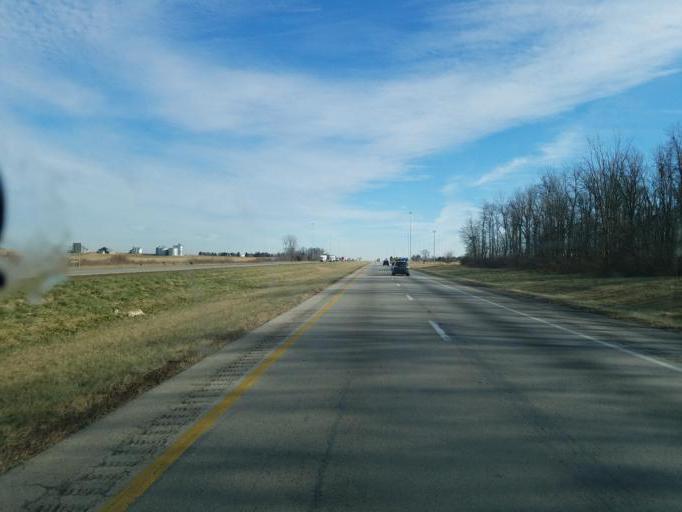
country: US
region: Ohio
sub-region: Preble County
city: New Paris
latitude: 39.8285
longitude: -84.7722
